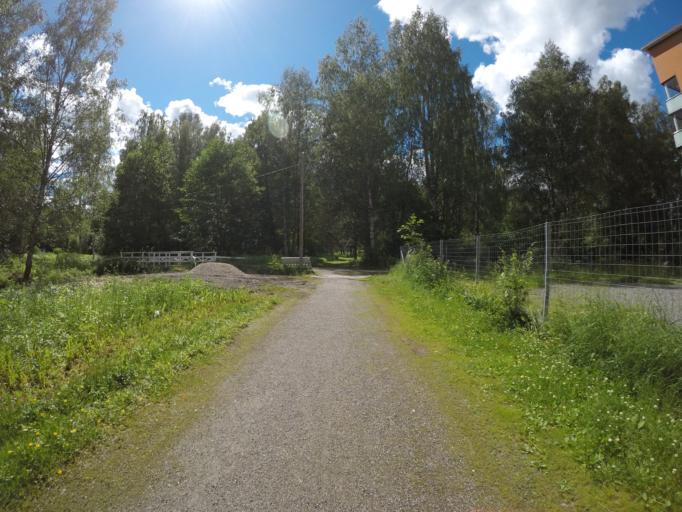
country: FI
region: Haeme
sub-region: Haemeenlinna
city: Haemeenlinna
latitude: 61.0002
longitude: 24.4562
